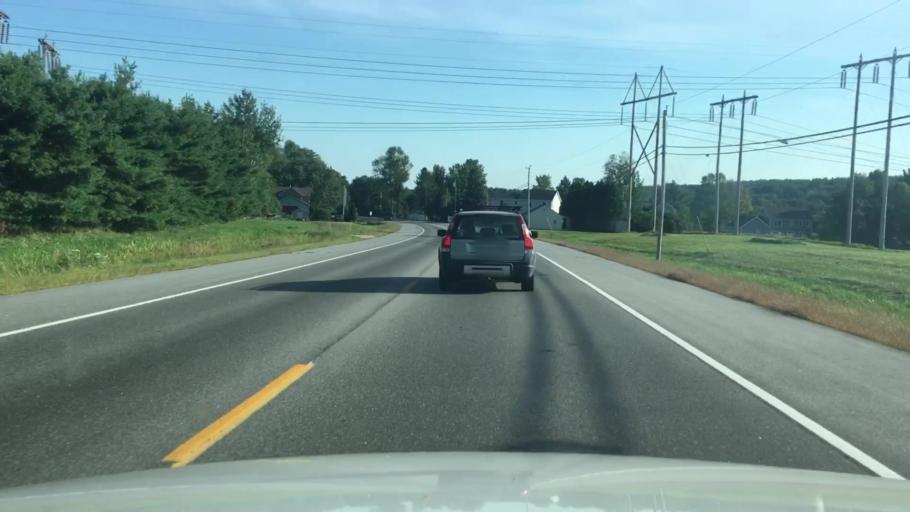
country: US
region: Maine
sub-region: Cumberland County
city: Cumberland Center
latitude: 43.7595
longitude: -70.3017
